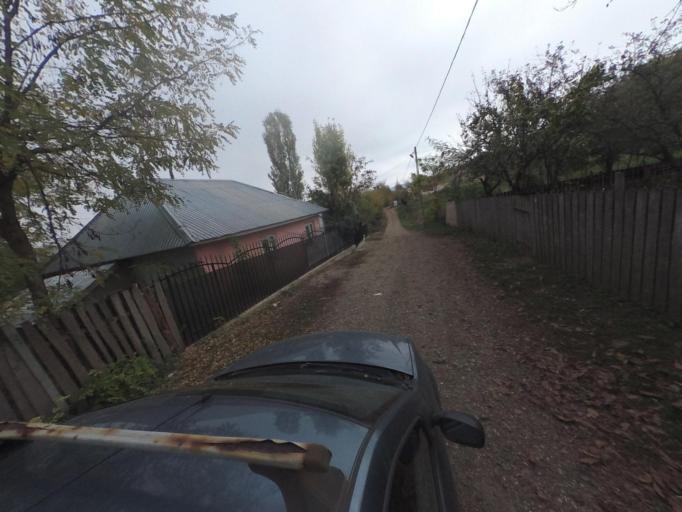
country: RO
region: Vaslui
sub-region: Comuna Bacesti
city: Bacesti
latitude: 46.8338
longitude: 27.2292
